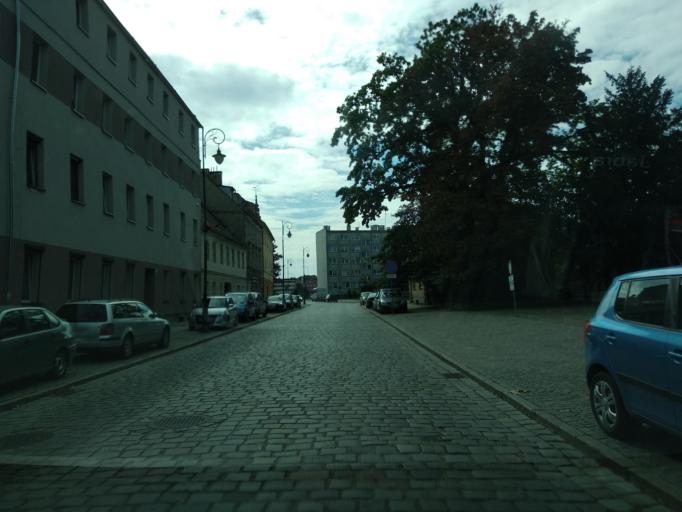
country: PL
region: Lower Silesian Voivodeship
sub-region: Powiat strzelinski
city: Strzelin
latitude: 50.7836
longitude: 17.0719
